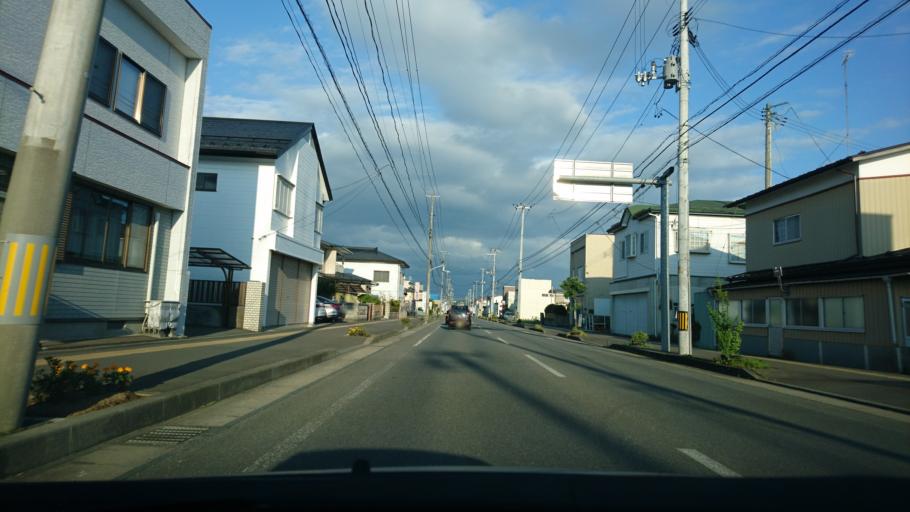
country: JP
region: Iwate
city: Ichinoseki
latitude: 38.9330
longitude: 141.1136
